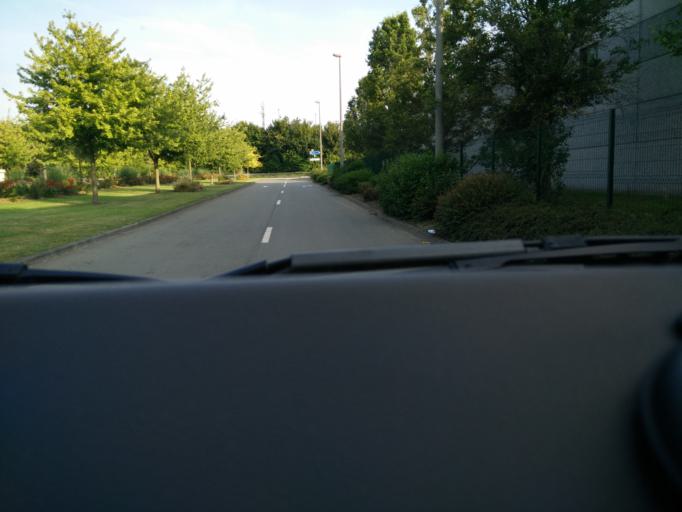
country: FR
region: Nord-Pas-de-Calais
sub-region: Departement du Nord
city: Wambrechies
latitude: 50.6799
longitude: 3.0504
